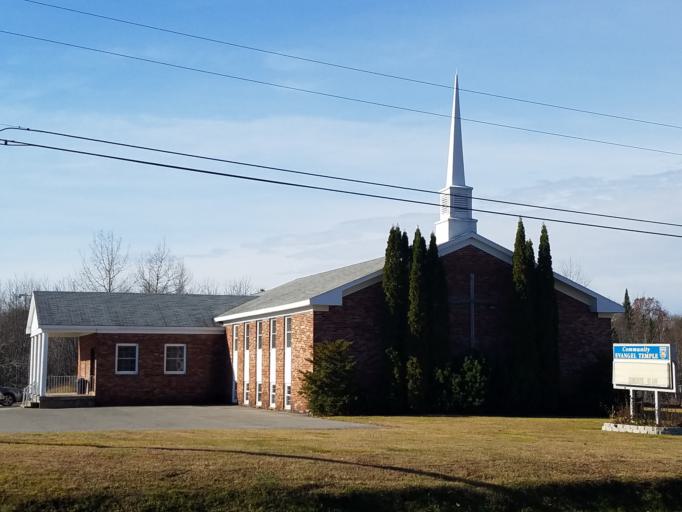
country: US
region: Maine
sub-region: Penobscot County
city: Lincoln
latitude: 45.3575
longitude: -68.5420
